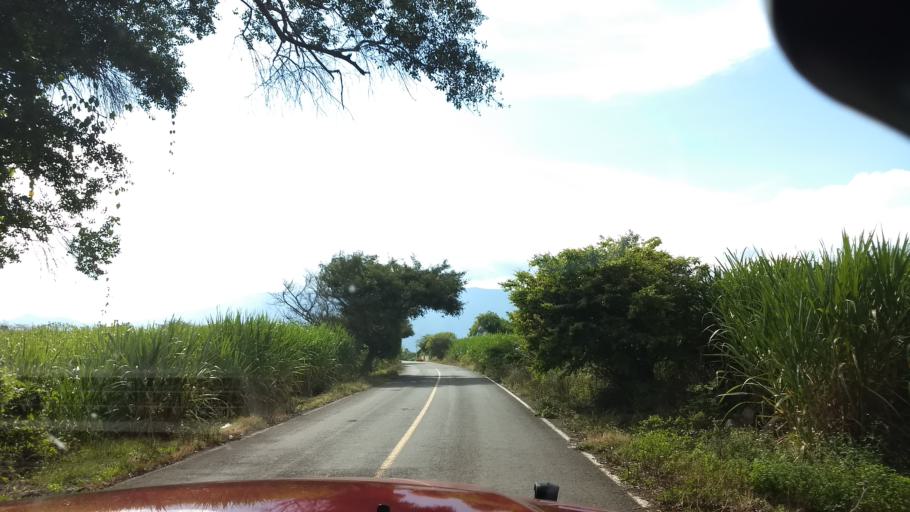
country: MX
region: Colima
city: Suchitlan
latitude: 19.4675
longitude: -103.7572
